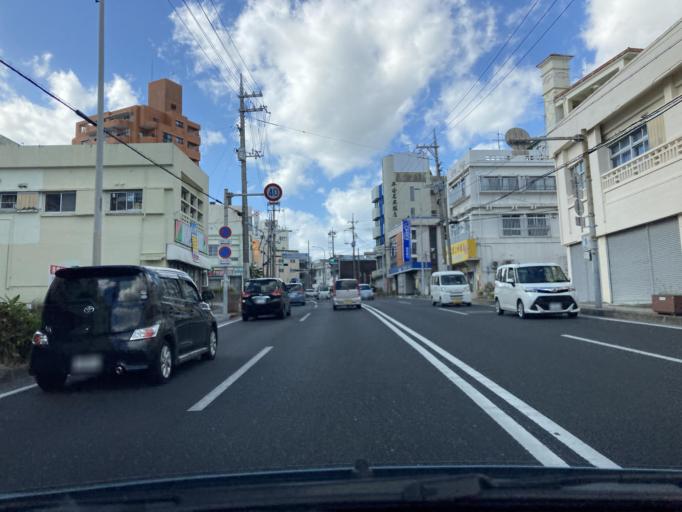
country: JP
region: Okinawa
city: Okinawa
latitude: 26.3376
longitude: 127.8032
